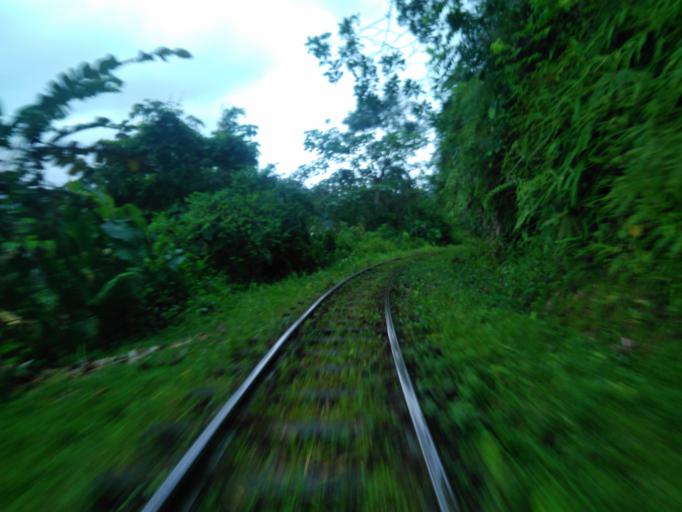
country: CO
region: Valle del Cauca
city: Buenaventura
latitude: 3.8422
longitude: -76.8702
